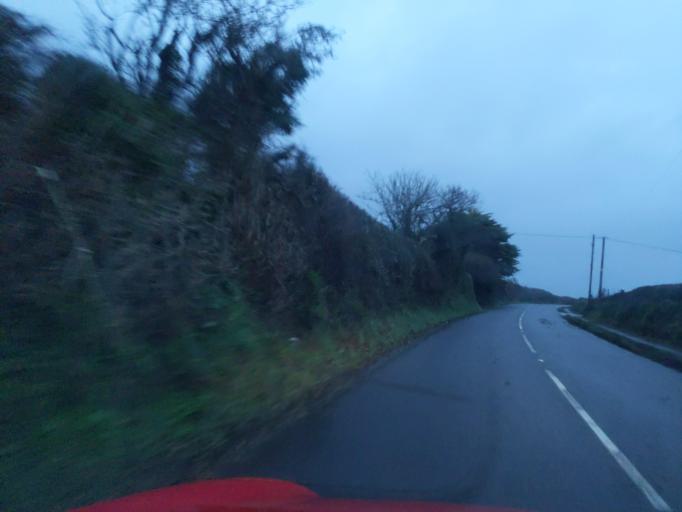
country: GB
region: England
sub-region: Cornwall
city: Saltash
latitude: 50.3671
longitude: -4.2578
